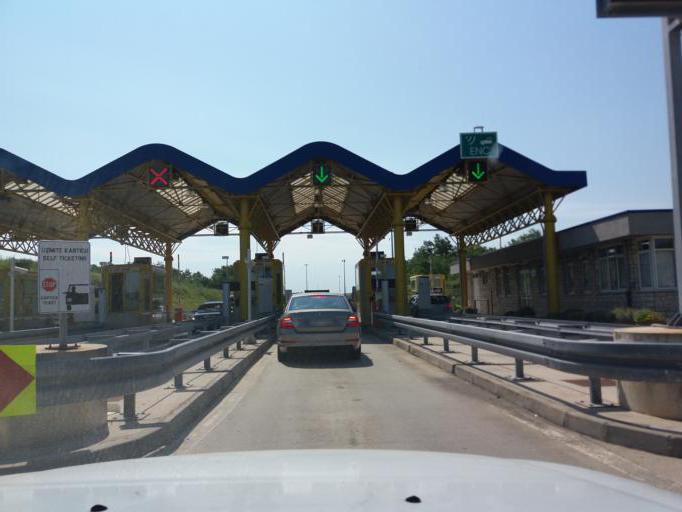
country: HR
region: Zadarska
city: Policnik
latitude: 44.1903
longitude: 15.4280
